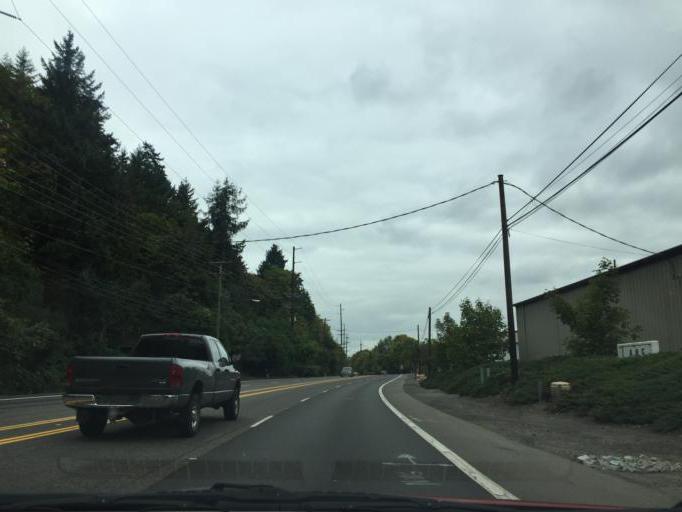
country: US
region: Oregon
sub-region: Washington County
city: West Haven
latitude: 45.5702
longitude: -122.7551
